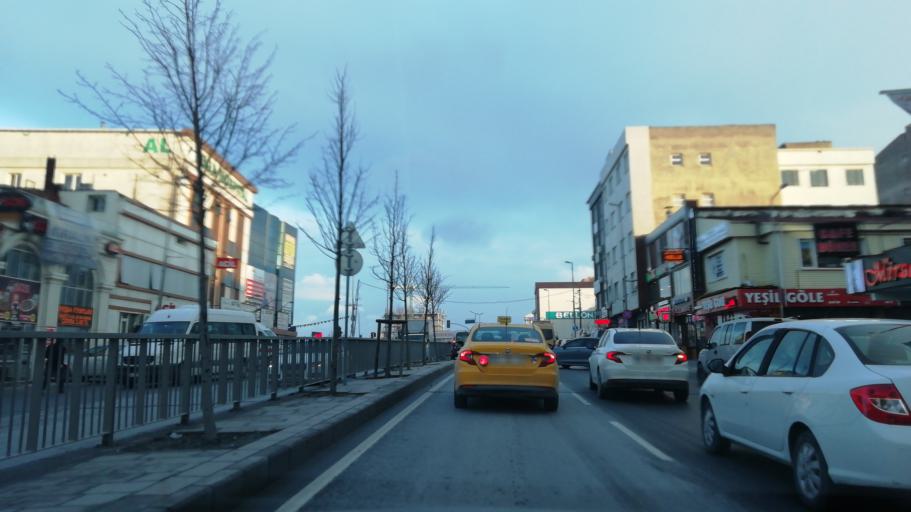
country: TR
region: Istanbul
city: Esenyurt
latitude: 41.0129
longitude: 28.6957
